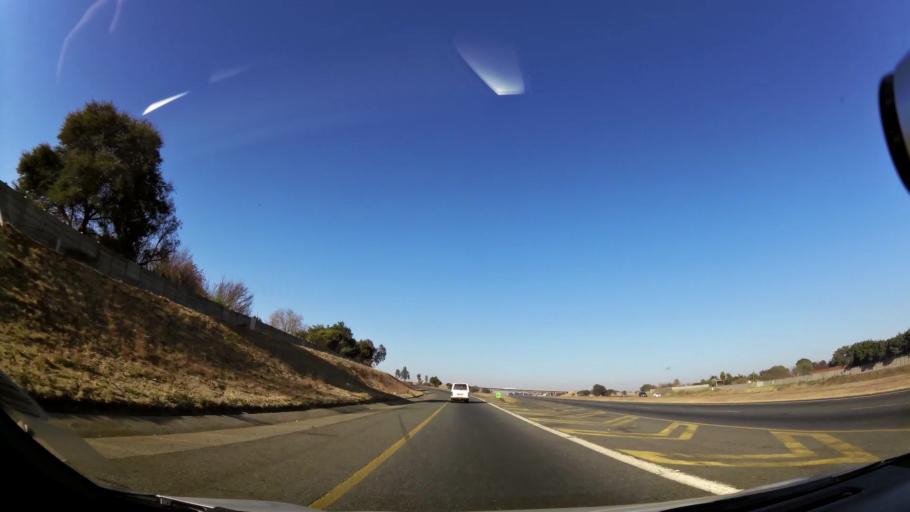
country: ZA
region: Gauteng
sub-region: Ekurhuleni Metropolitan Municipality
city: Germiston
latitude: -26.3470
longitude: 28.1026
